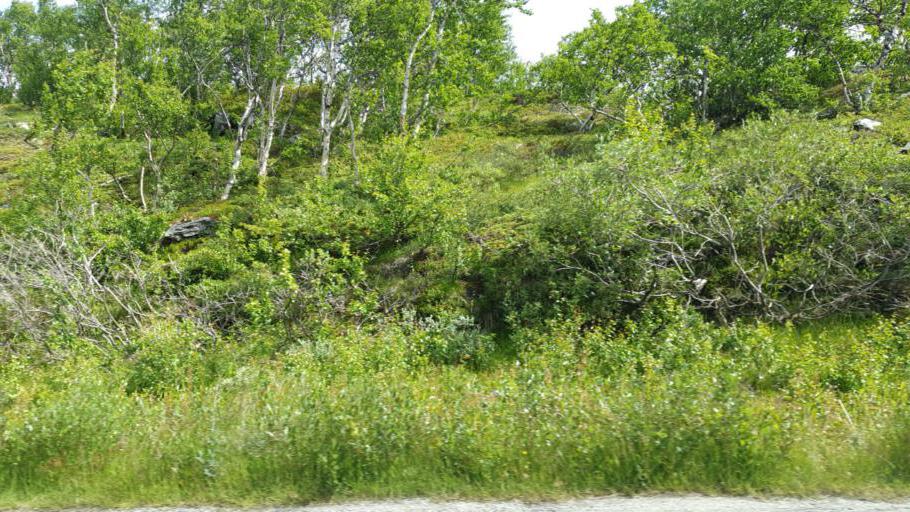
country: NO
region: Oppland
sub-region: Lom
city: Fossbergom
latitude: 61.4908
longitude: 8.8180
